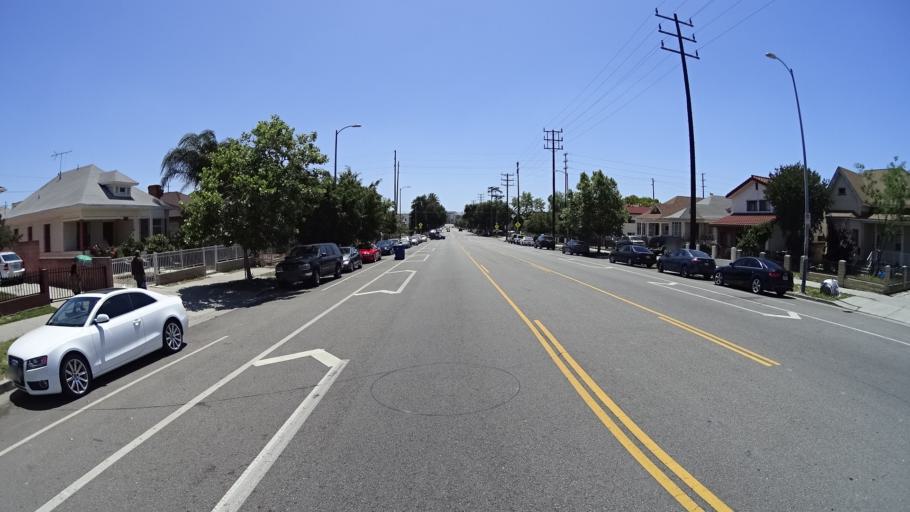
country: US
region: California
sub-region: Los Angeles County
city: Los Angeles
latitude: 34.0729
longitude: -118.2117
